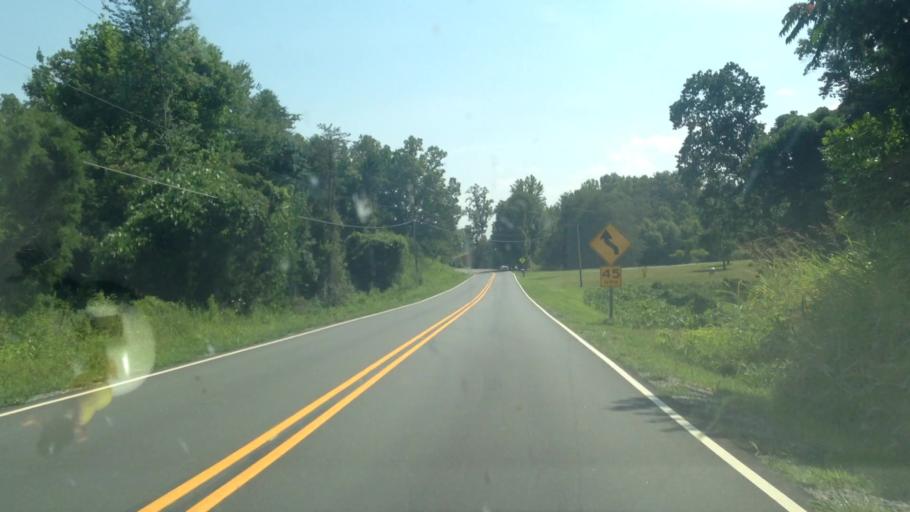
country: US
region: North Carolina
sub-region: Stokes County
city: Danbury
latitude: 36.4103
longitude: -80.0910
